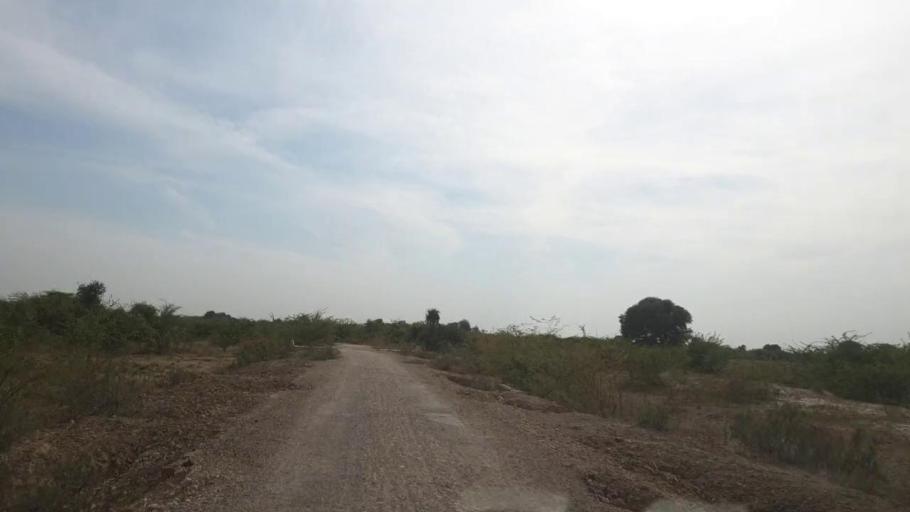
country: PK
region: Sindh
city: Nabisar
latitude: 25.0073
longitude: 69.5607
